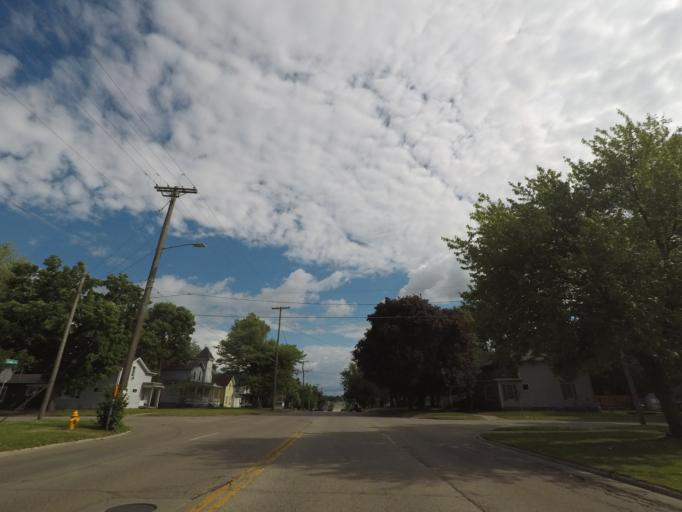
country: US
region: Wisconsin
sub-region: Rock County
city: Janesville
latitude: 42.6755
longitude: -89.0318
